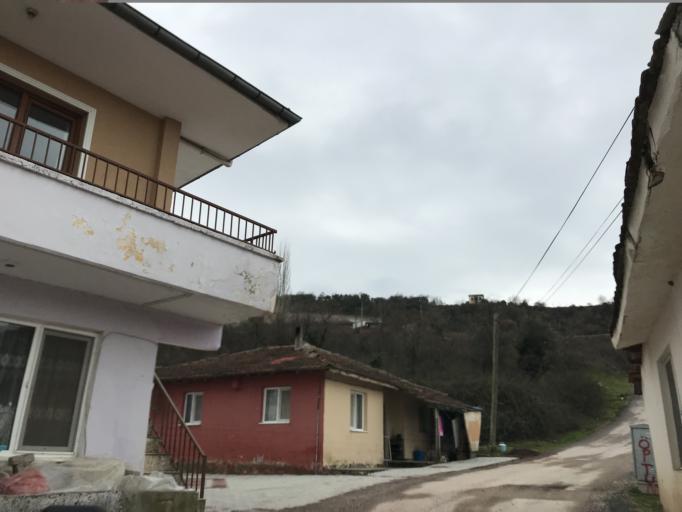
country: TR
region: Yalova
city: Termal
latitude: 40.5964
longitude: 29.1715
